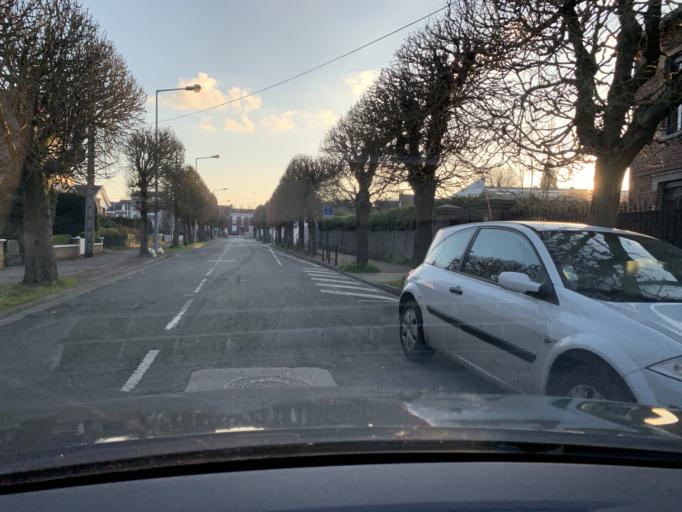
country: FR
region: Nord-Pas-de-Calais
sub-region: Departement du Nord
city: Douai
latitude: 50.3596
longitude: 3.0823
